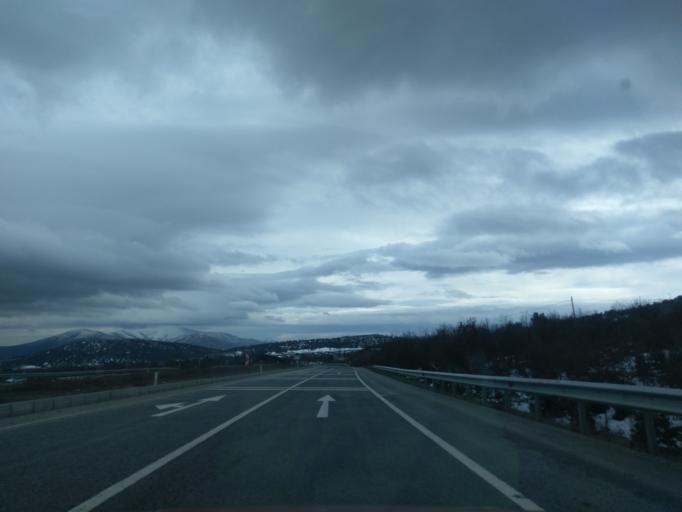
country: TR
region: Kuetahya
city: Aslanapa
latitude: 39.2757
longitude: 29.9167
